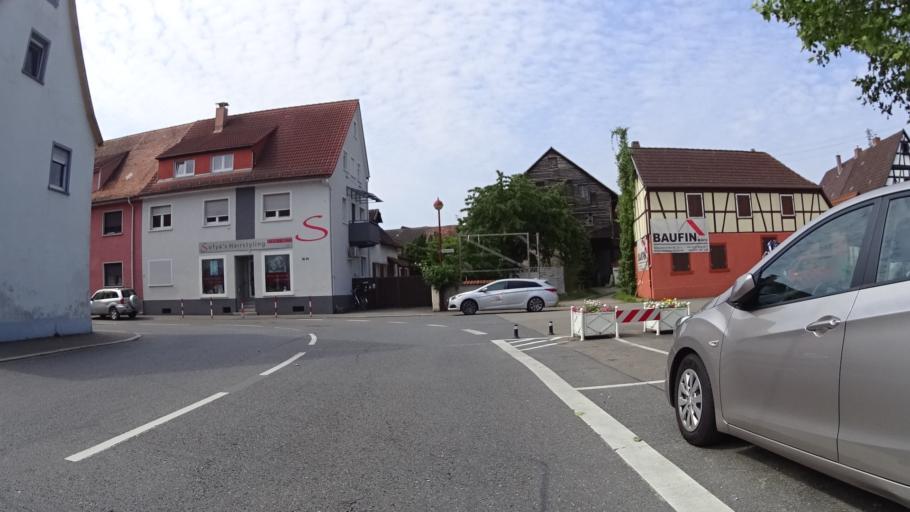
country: DE
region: Baden-Wuerttemberg
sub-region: Karlsruhe Region
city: Graben-Neudorf
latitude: 49.1586
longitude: 8.4829
